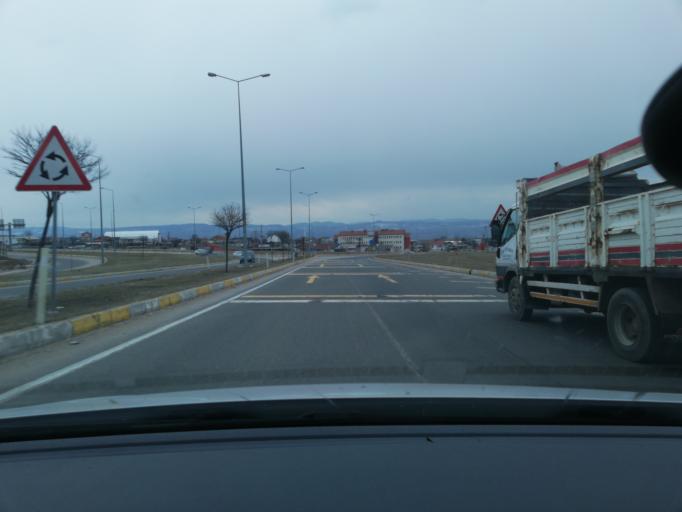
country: TR
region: Bolu
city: Gerede
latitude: 40.7925
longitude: 32.2072
